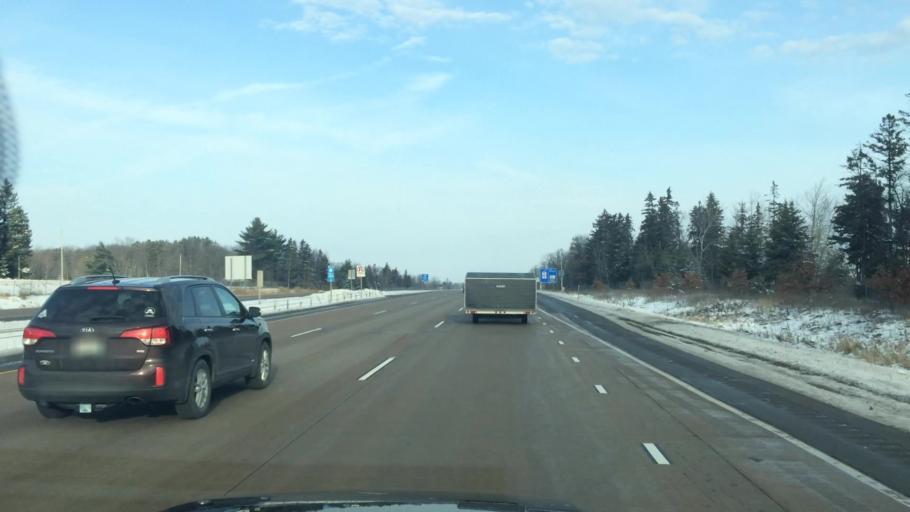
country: US
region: Wisconsin
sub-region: Marathon County
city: Rib Mountain
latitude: 44.9175
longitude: -89.6548
